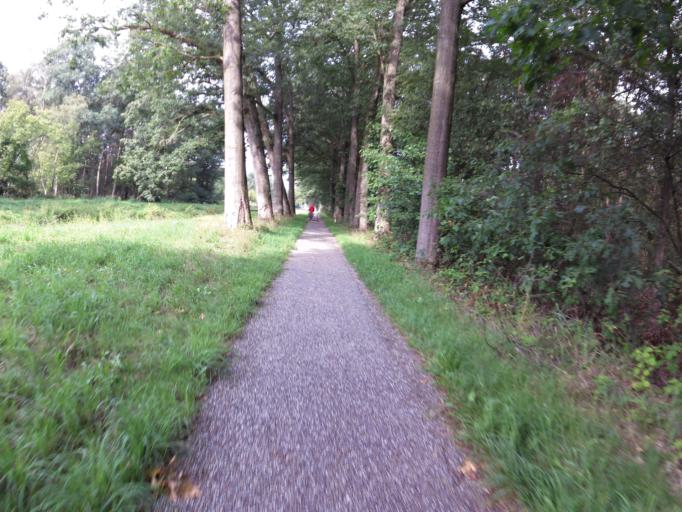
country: NL
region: Gelderland
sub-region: Oude IJsselstreek
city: Varsseveld
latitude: 51.9635
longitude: 6.4330
